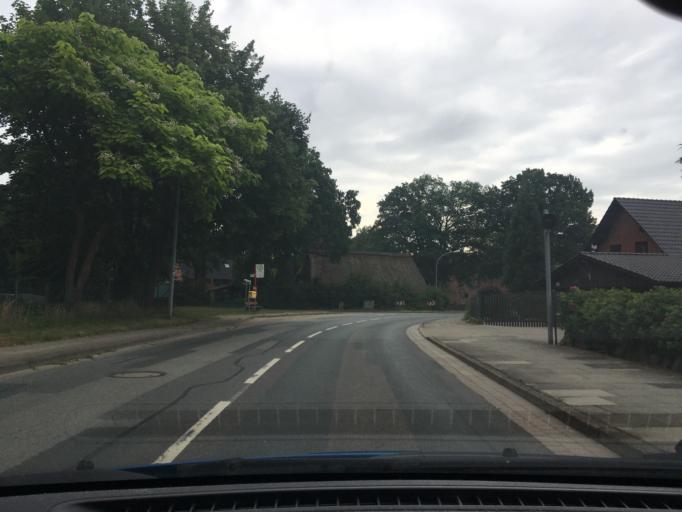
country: DE
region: Lower Saxony
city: Wenzendorf
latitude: 53.3486
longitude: 9.7550
